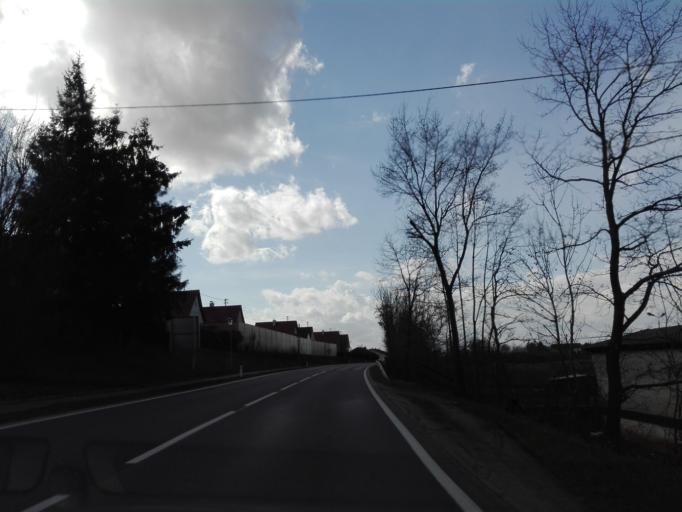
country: AT
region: Upper Austria
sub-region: Politischer Bezirk Urfahr-Umgebung
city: Goldworth
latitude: 48.2858
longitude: 14.0991
